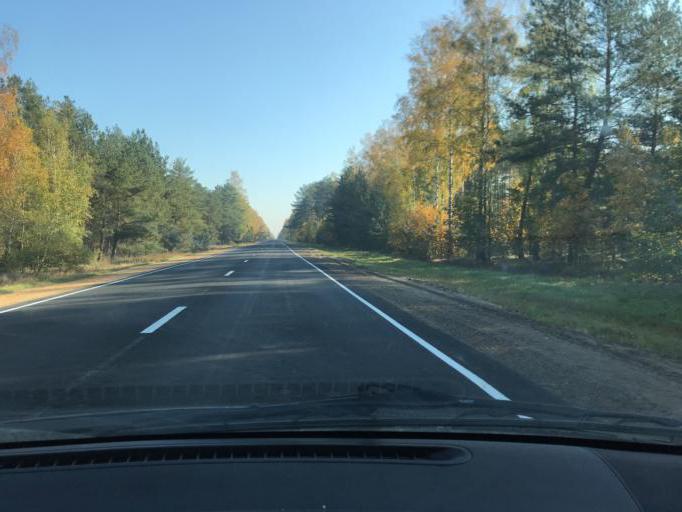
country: BY
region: Brest
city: Baranovichi
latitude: 52.9035
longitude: 25.8895
